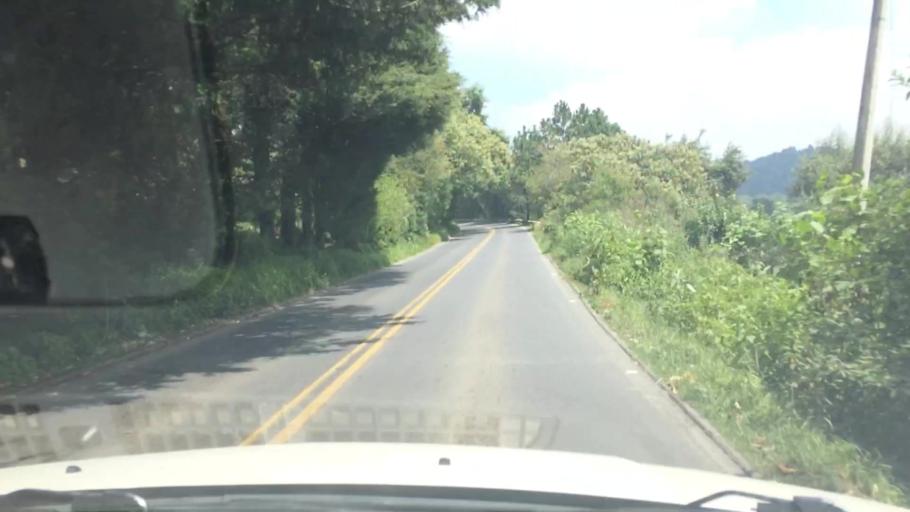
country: MX
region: Mexico City
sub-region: Tlalpan
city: Lomas de Tepemecatl
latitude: 19.2295
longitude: -99.2150
